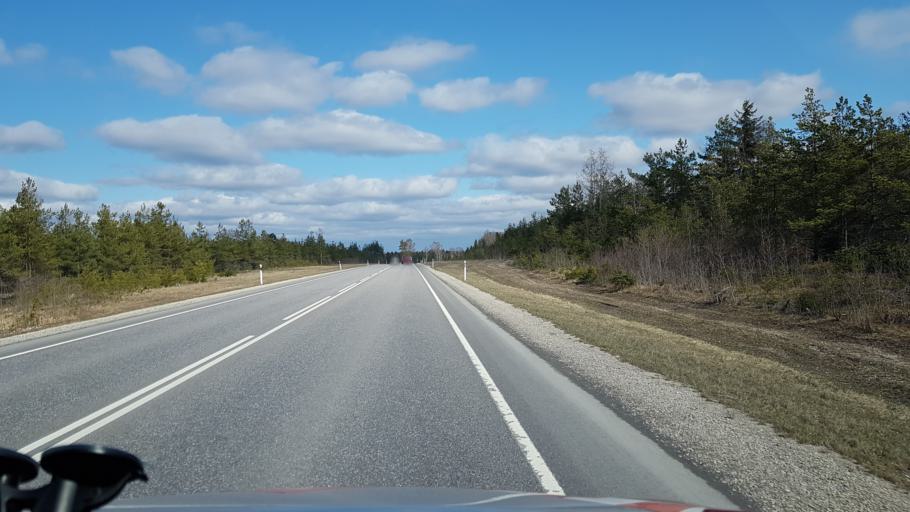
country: EE
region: Harju
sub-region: Nissi vald
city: Turba
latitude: 58.9762
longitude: 23.9534
